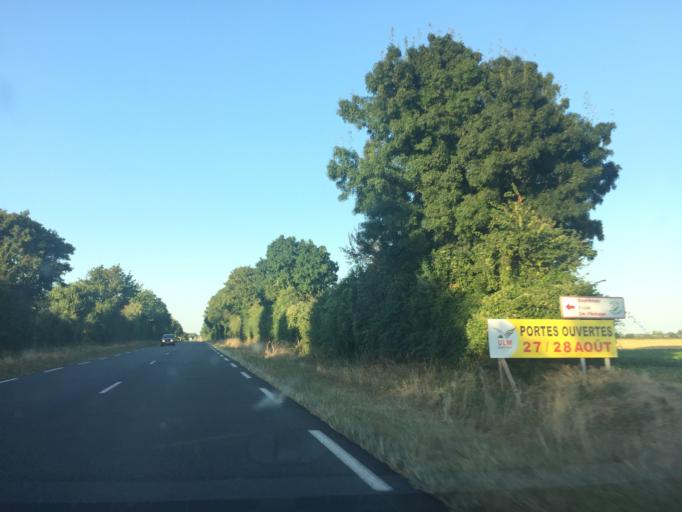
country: FR
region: Poitou-Charentes
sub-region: Departement des Deux-Sevres
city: Pamproux
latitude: 46.3401
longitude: -0.0176
